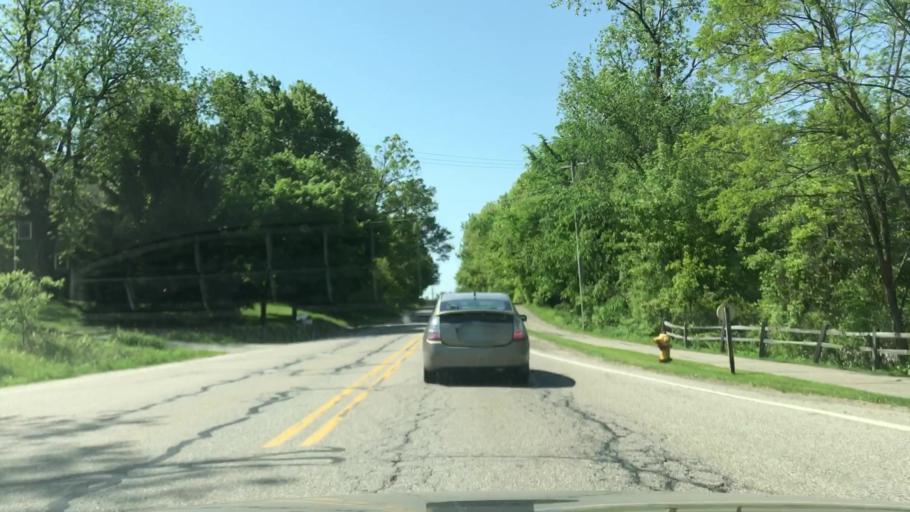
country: US
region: Michigan
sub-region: Kent County
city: Forest Hills
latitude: 42.9245
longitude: -85.5400
